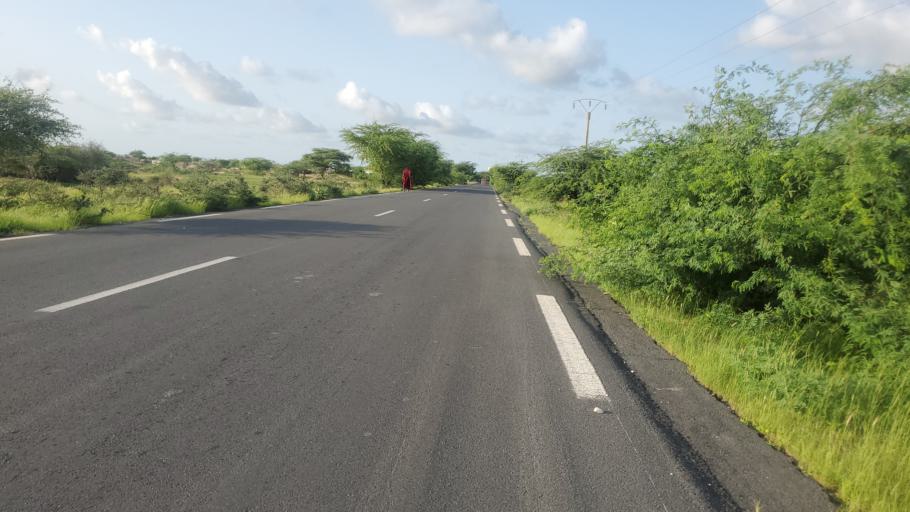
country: SN
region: Saint-Louis
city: Saint-Louis
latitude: 16.1293
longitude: -16.4127
